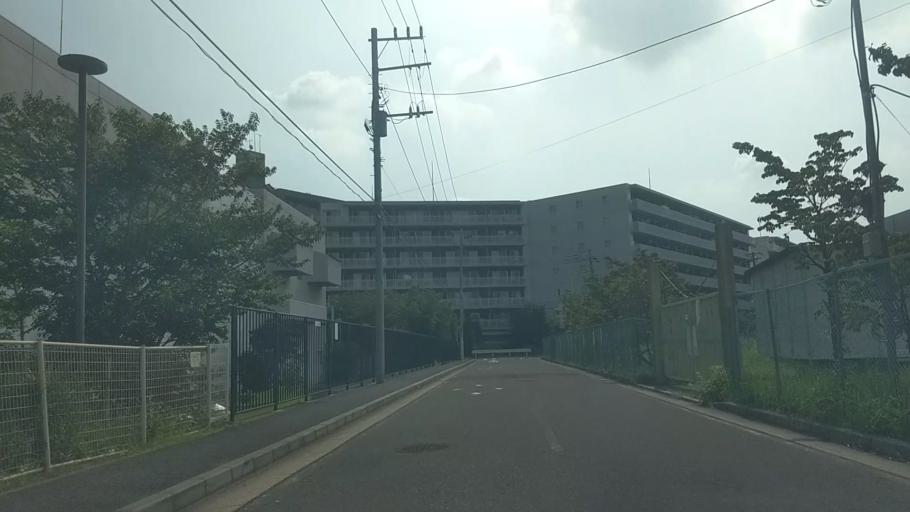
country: JP
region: Kanagawa
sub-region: Kawasaki-shi
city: Kawasaki
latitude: 35.5192
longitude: 139.6785
